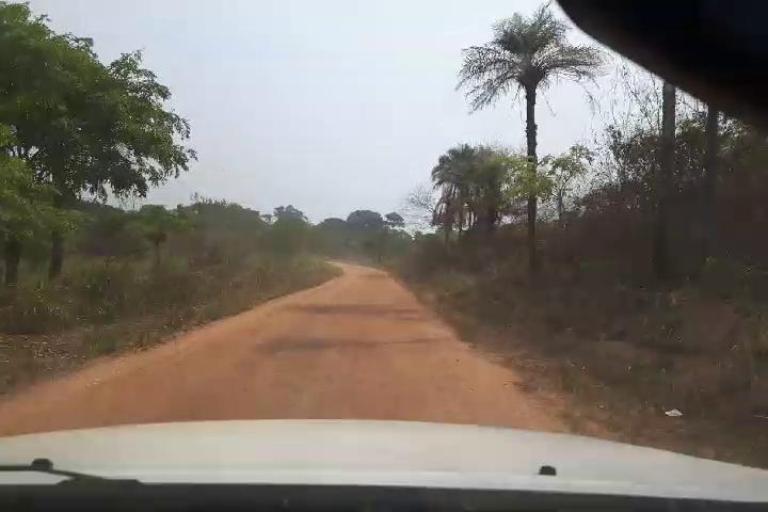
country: SL
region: Northern Province
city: Masingbi
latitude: 8.8816
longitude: -11.8200
